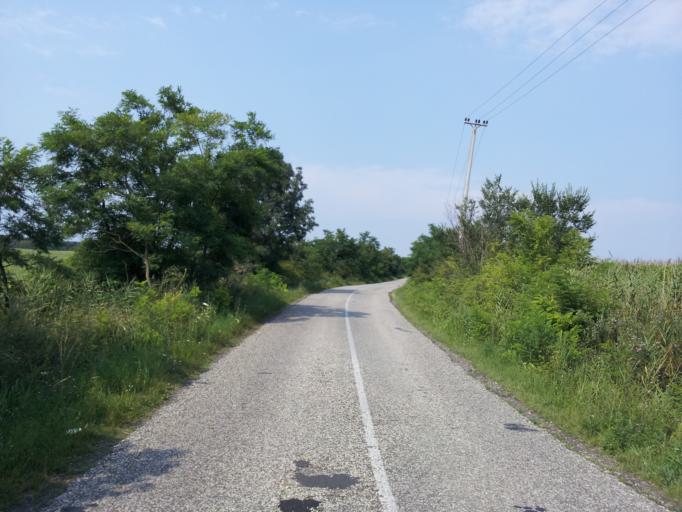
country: HU
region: Pest
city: Szigetujfalu
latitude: 47.2145
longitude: 18.9188
